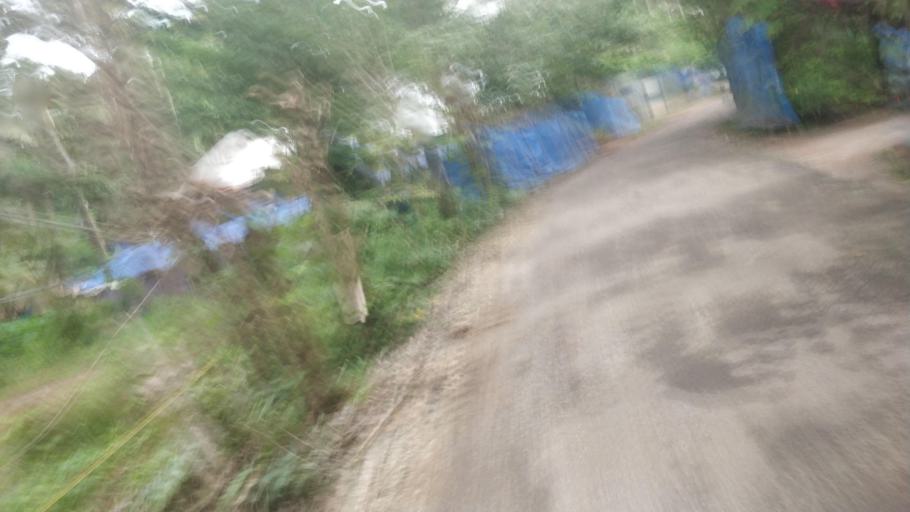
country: IN
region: Kerala
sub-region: Alappuzha
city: Vayalar
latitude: 9.7055
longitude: 76.3528
